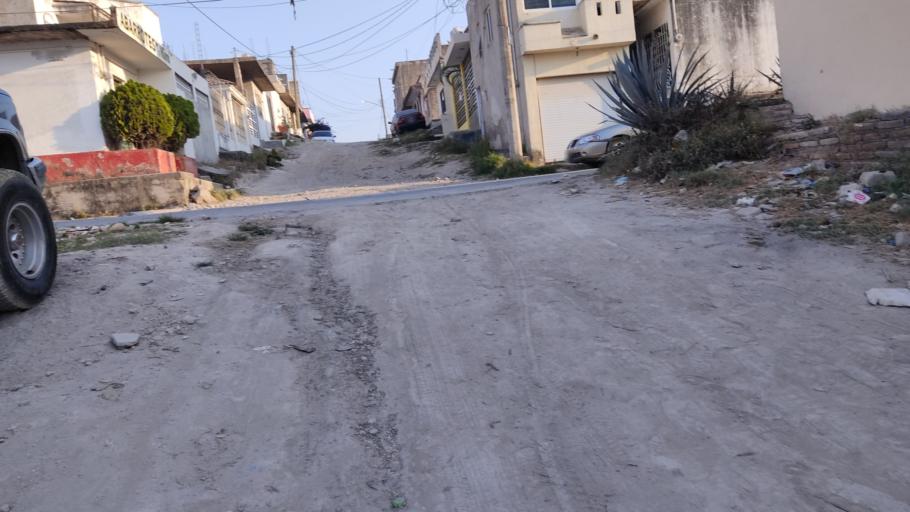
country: MX
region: Nayarit
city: Tepic
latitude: 21.5145
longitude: -104.8732
